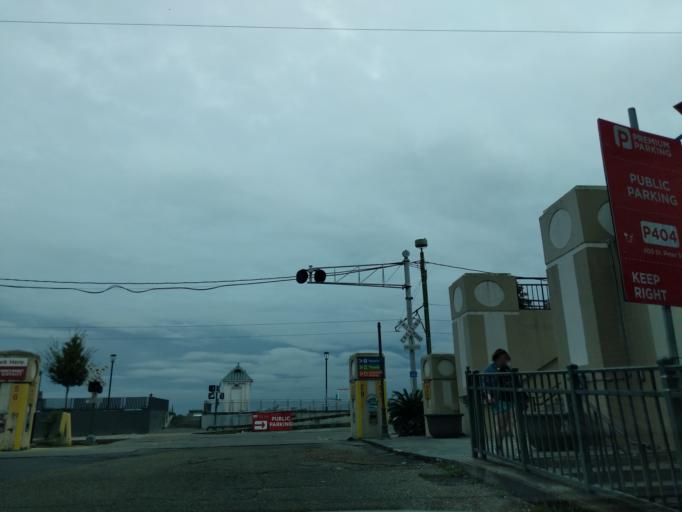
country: US
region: Louisiana
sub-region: Orleans Parish
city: New Orleans
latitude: 29.9565
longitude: -90.0625
